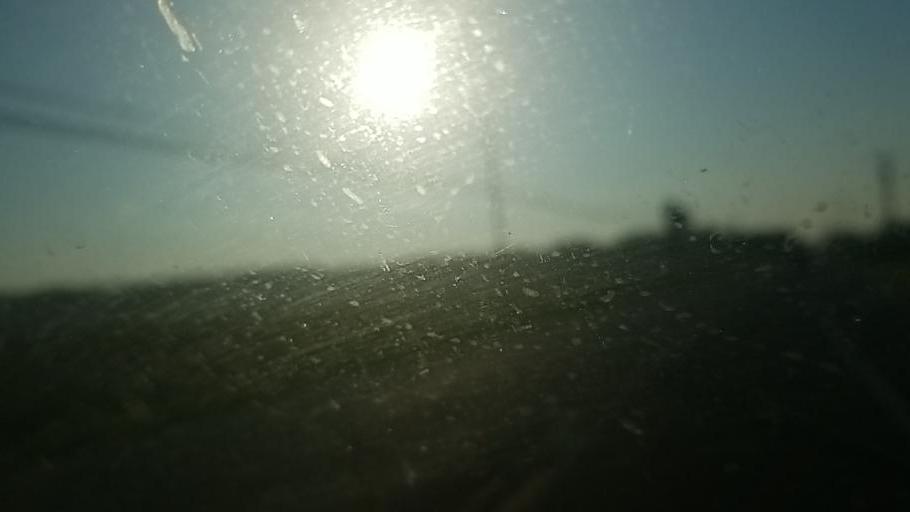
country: US
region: Maryland
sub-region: Worcester County
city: Ocean Pines
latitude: 38.4636
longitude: -75.1461
